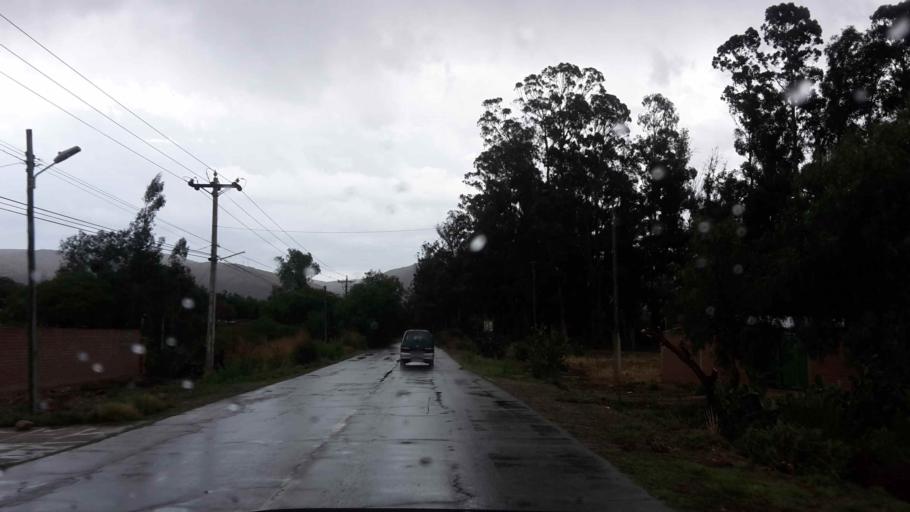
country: BO
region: Cochabamba
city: Tarata
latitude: -17.5439
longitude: -66.1051
